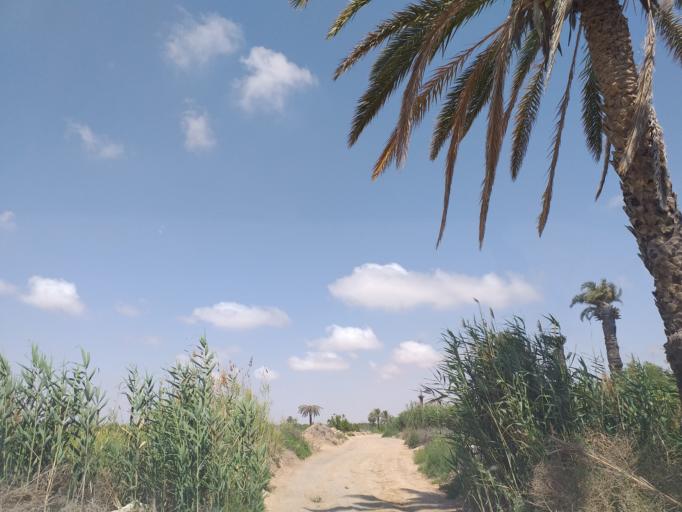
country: TN
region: Qabis
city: Gabes
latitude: 33.9516
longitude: 10.0491
